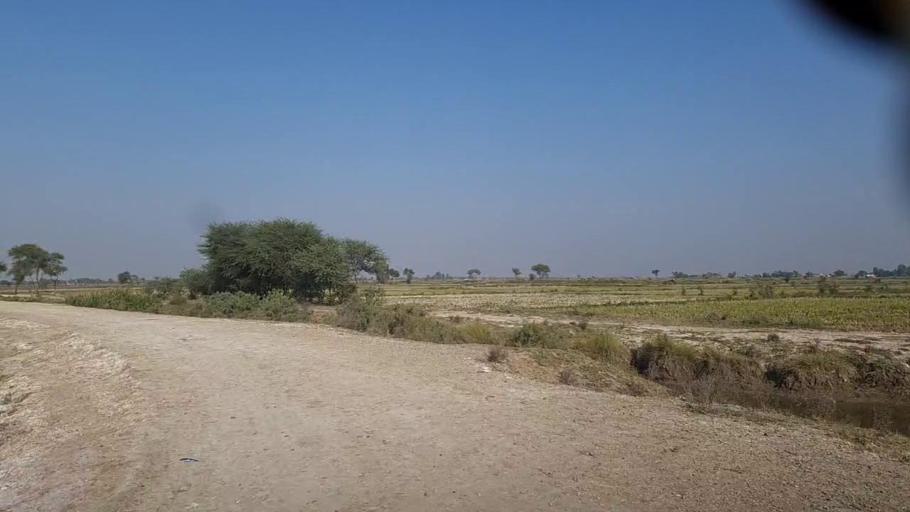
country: PK
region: Sindh
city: Jacobabad
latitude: 28.3058
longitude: 68.6080
